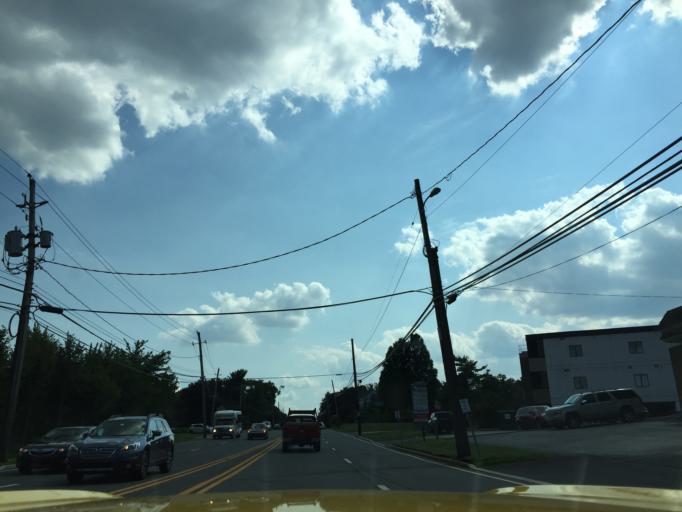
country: US
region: Delaware
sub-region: New Castle County
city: Bellefonte
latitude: 39.7882
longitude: -75.5343
